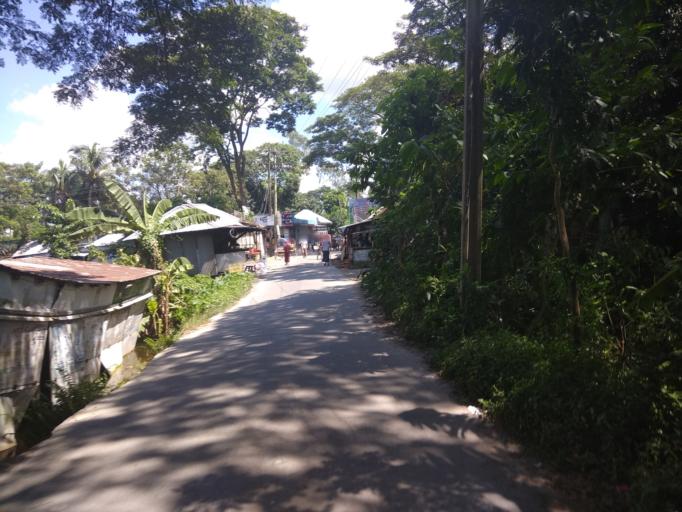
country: BD
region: Dhaka
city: Narayanganj
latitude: 23.4413
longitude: 90.4891
